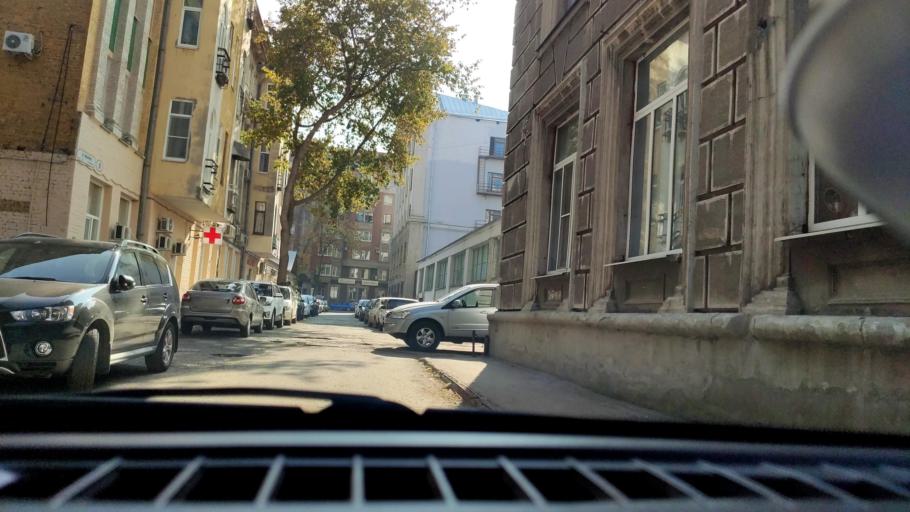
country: RU
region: Samara
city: Samara
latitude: 53.2012
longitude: 50.1152
